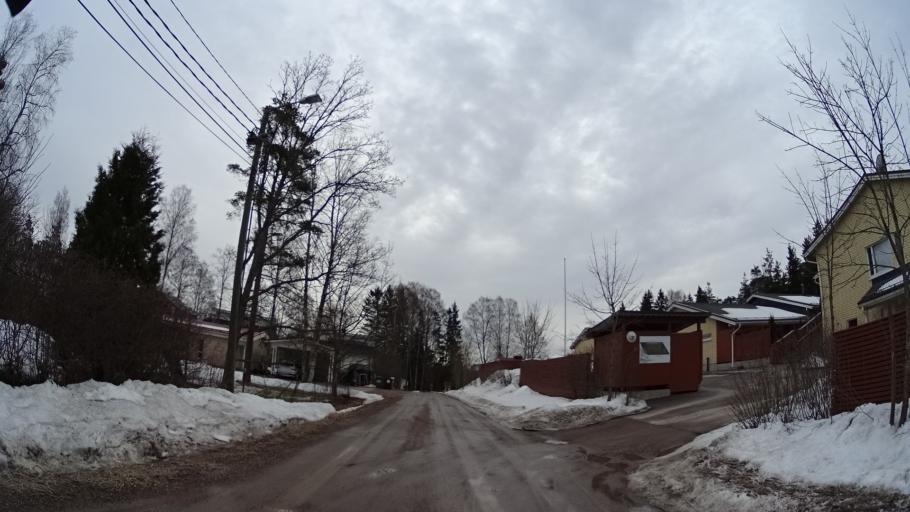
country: FI
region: Uusimaa
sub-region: Helsinki
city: Teekkarikylae
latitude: 60.2312
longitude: 24.8360
